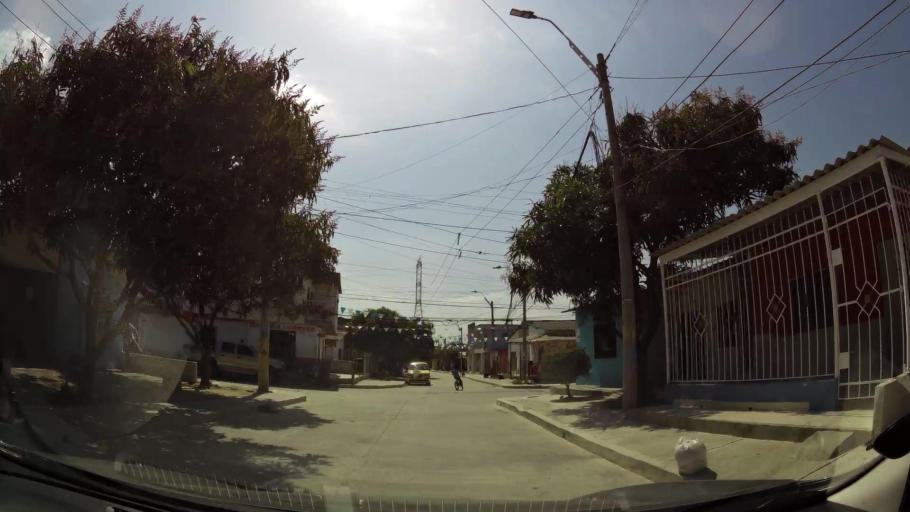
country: CO
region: Atlantico
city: Barranquilla
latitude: 10.9693
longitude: -74.8368
